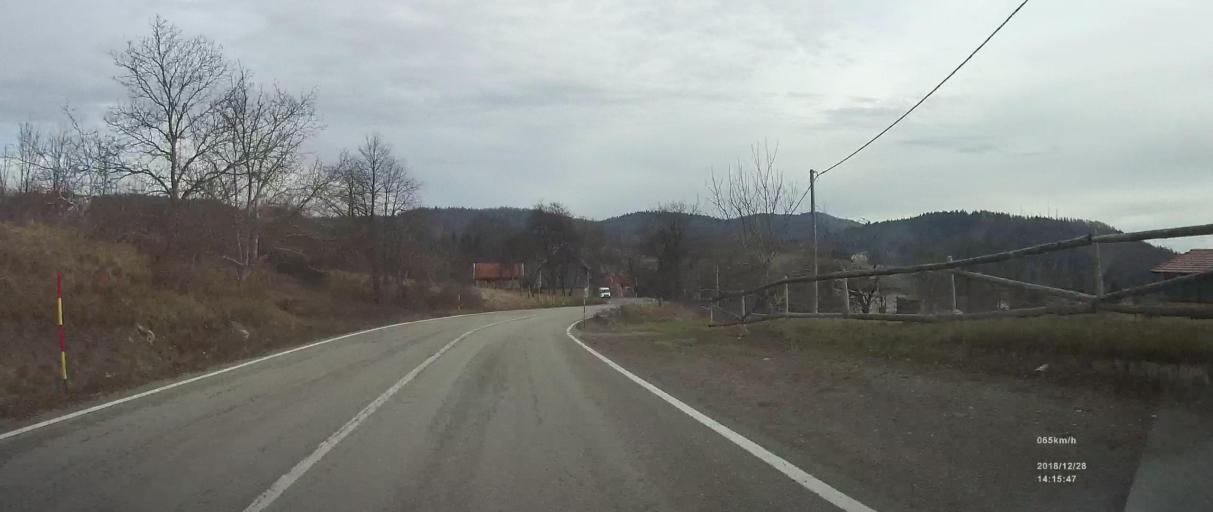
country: HR
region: Primorsko-Goranska
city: Vrbovsko
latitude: 45.4220
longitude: 15.0295
